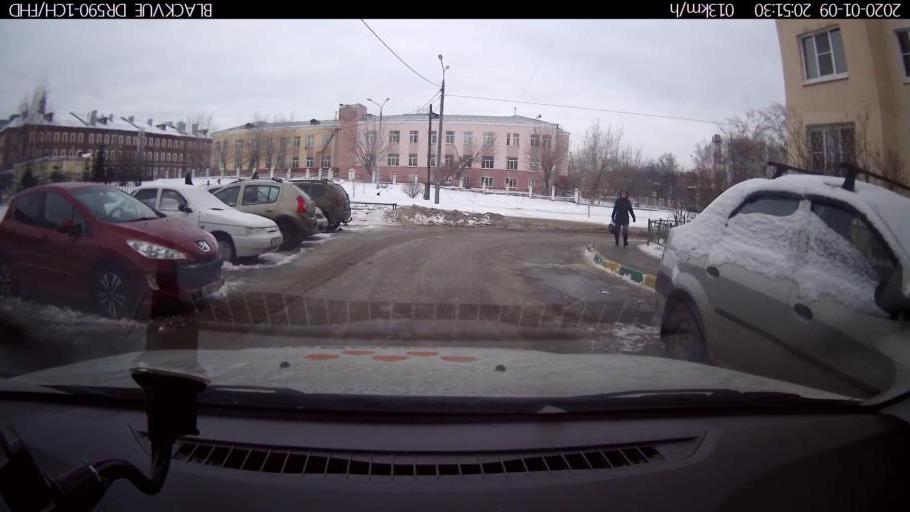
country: RU
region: Nizjnij Novgorod
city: Nizhniy Novgorod
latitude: 56.2919
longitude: 43.9432
